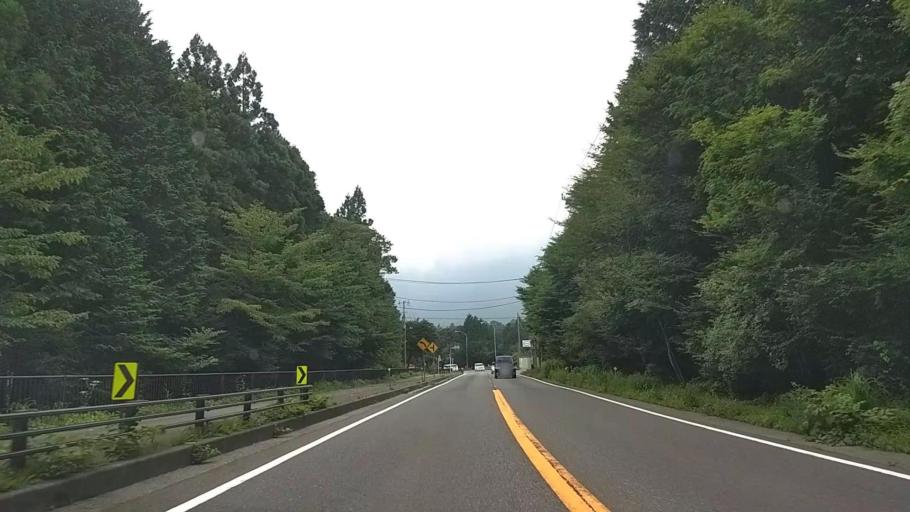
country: JP
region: Yamanashi
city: Fujikawaguchiko
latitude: 35.4295
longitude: 138.5932
